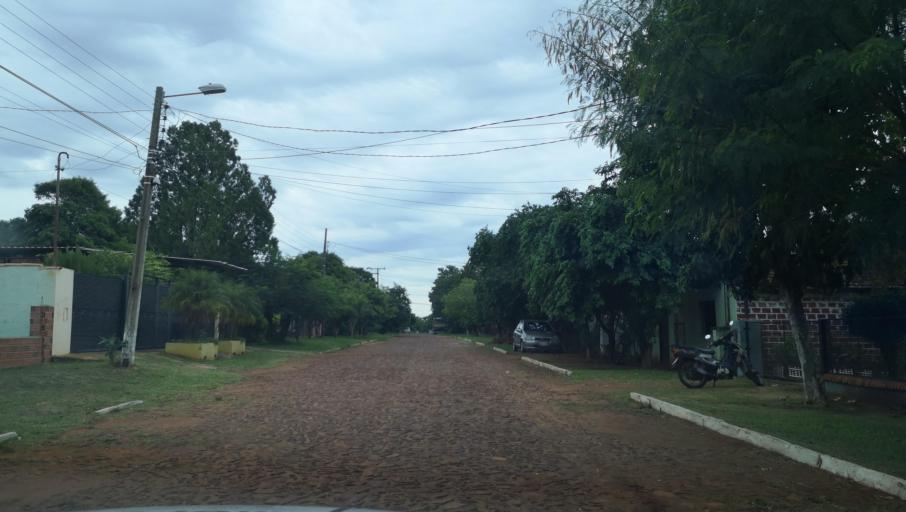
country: PY
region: Misiones
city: Santa Maria
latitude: -26.8900
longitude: -57.0399
